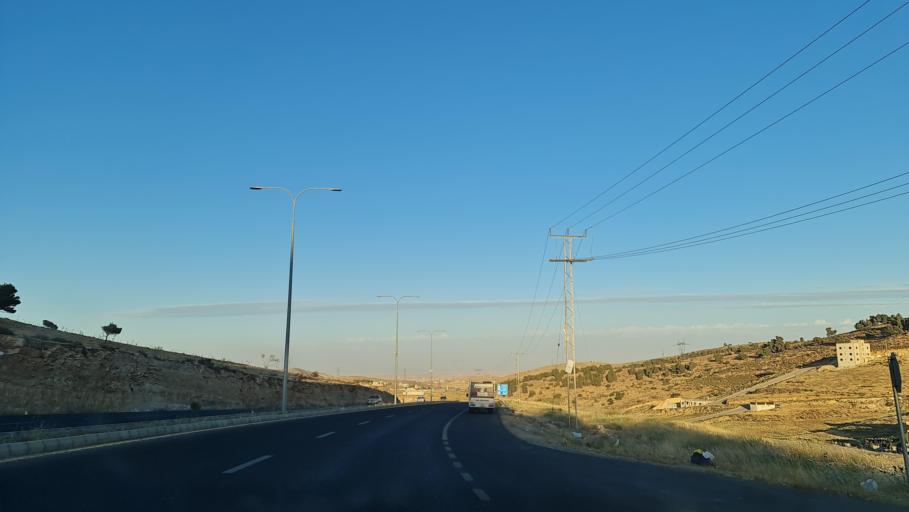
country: JO
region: Zarqa
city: Russeifa
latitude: 32.0926
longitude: 35.9688
